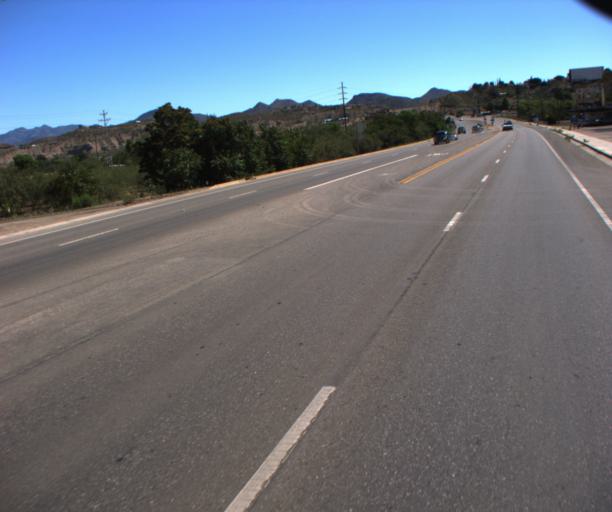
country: US
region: Arizona
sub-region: Gila County
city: Claypool
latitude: 33.4148
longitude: -110.8333
